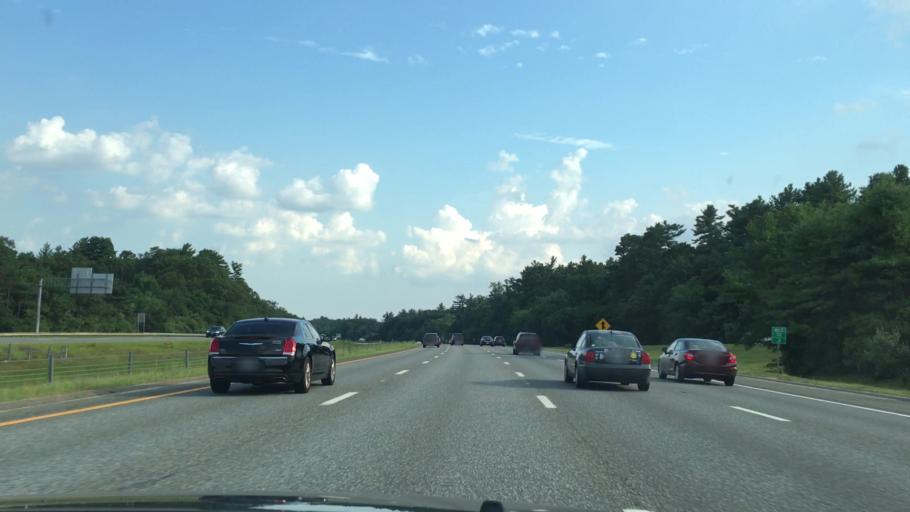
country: US
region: Massachusetts
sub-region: Essex County
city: Topsfield
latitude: 42.6256
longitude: -70.9791
